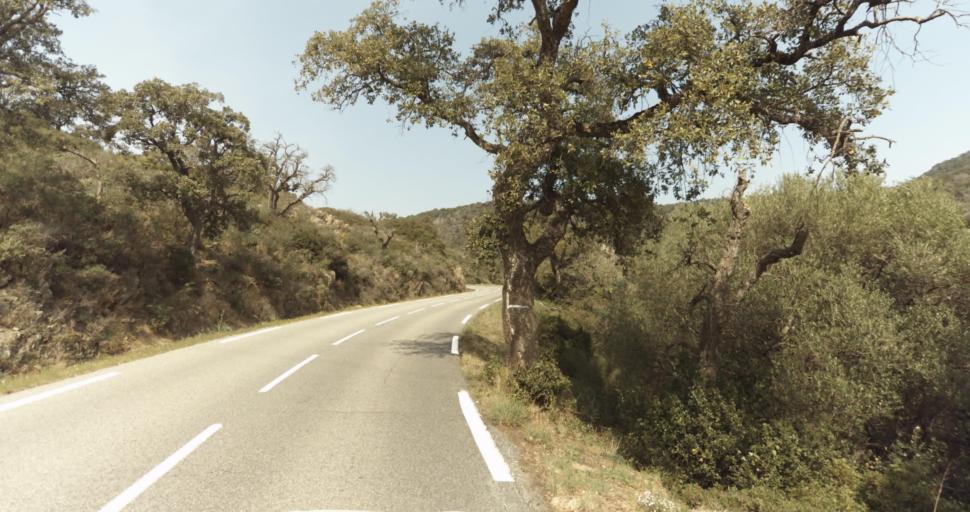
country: FR
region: Provence-Alpes-Cote d'Azur
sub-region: Departement du Var
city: Bormes-les-Mimosas
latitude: 43.1590
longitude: 6.3438
